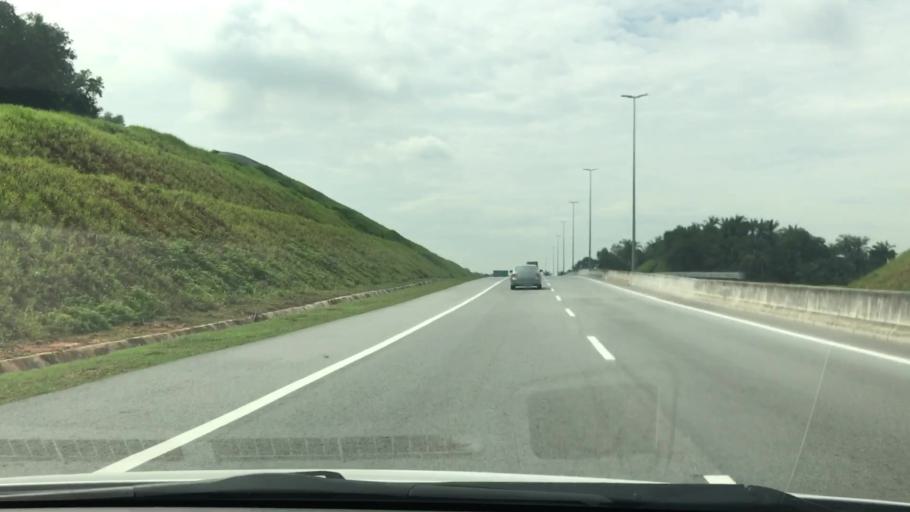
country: MY
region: Selangor
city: Kampong Baharu Balakong
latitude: 3.0085
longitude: 101.6873
